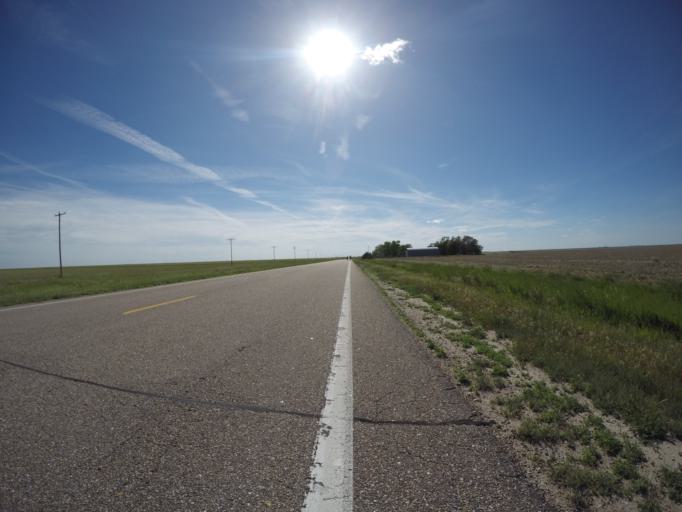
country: US
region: Kansas
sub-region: Cheyenne County
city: Saint Francis
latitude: 39.7566
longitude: -101.9909
